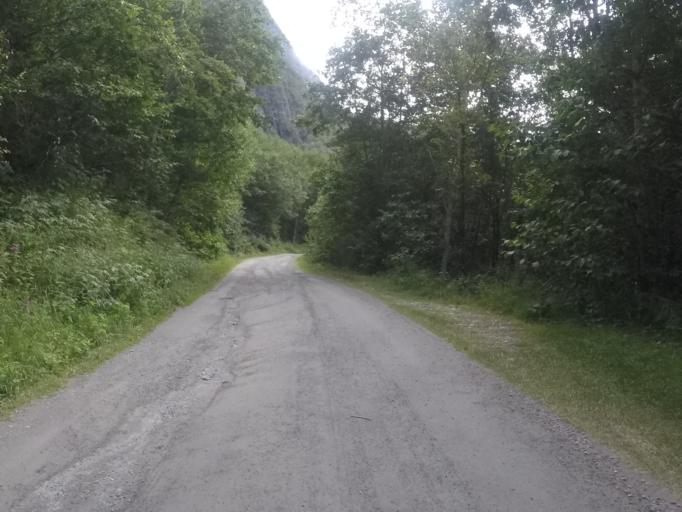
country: NO
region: Sogn og Fjordane
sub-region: Stryn
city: Stryn
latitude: 61.7625
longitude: 7.0415
